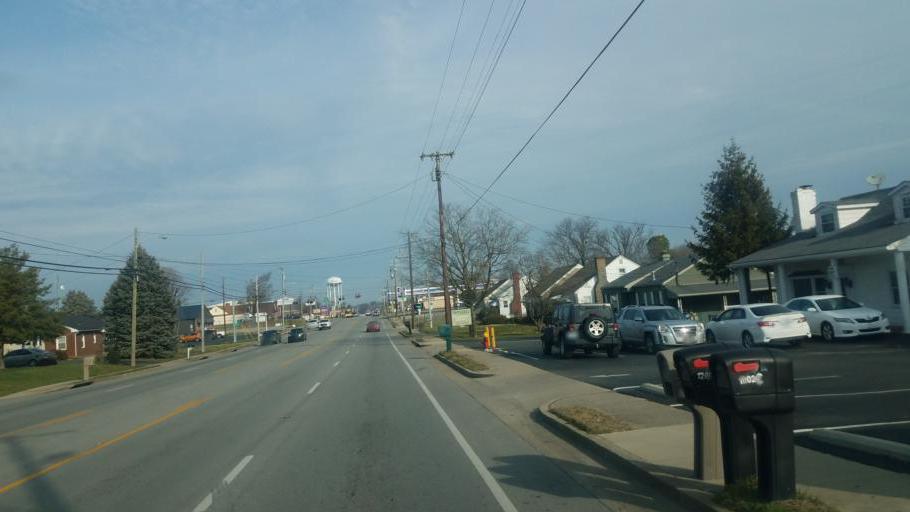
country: US
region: Kentucky
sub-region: Boyle County
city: Danville
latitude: 37.6245
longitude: -84.7746
